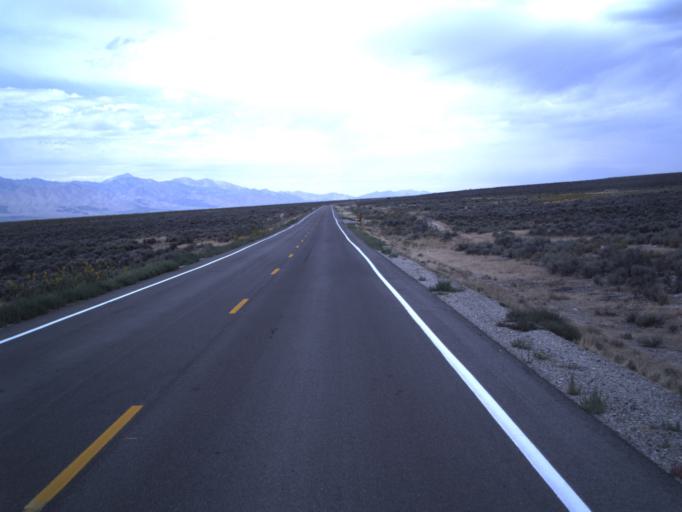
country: US
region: Utah
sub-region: Tooele County
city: Tooele
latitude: 40.2841
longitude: -112.2621
